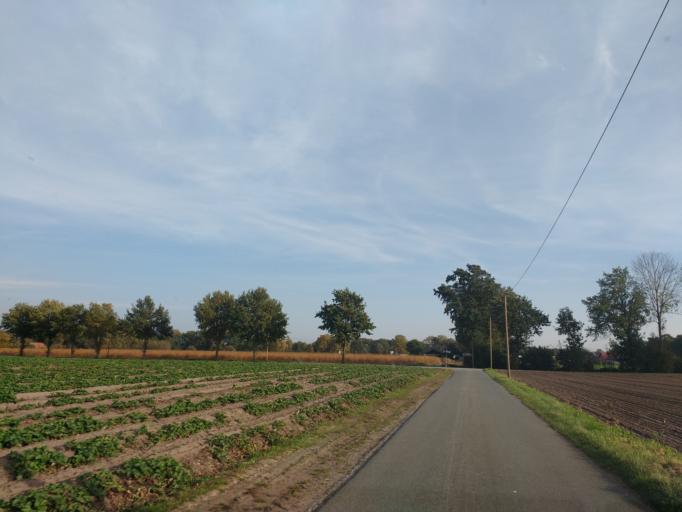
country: DE
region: North Rhine-Westphalia
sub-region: Regierungsbezirk Detmold
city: Hovelhof
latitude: 51.7649
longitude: 8.6453
